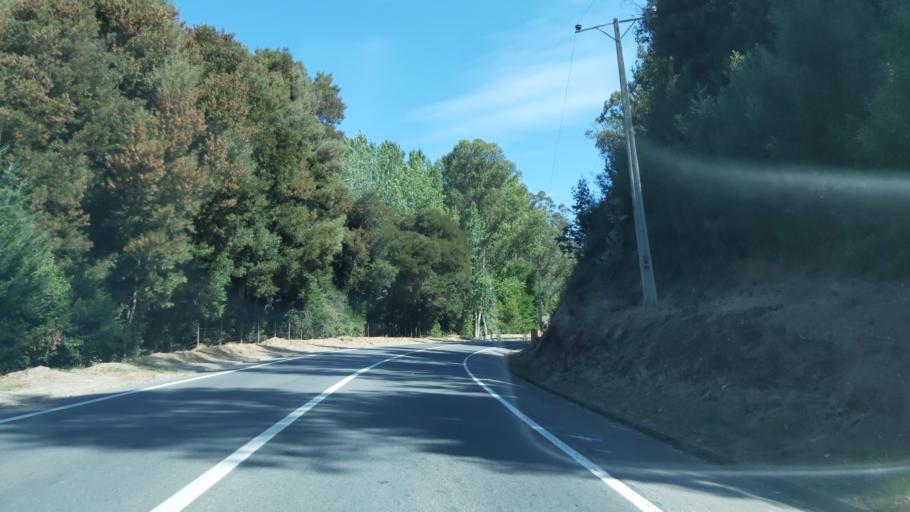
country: CL
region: Biobio
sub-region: Provincia de Concepcion
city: Lota
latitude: -37.1205
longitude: -72.9850
